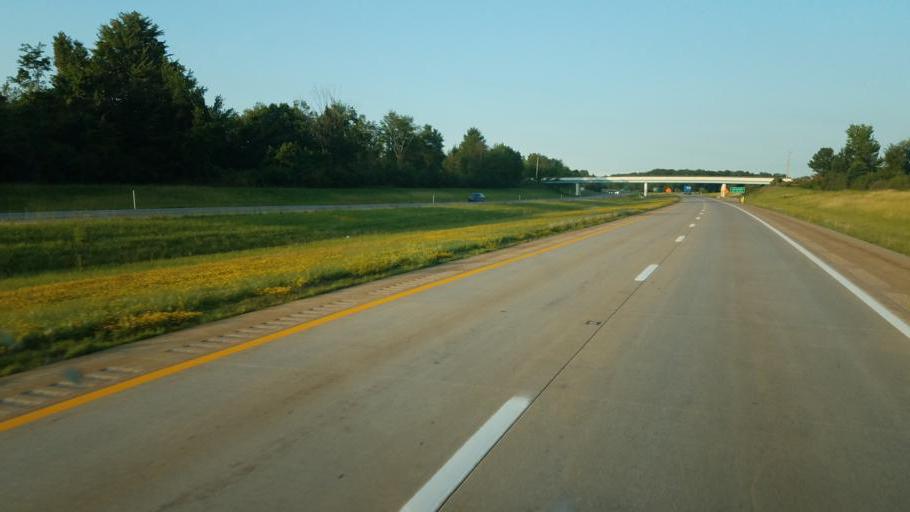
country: US
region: Ohio
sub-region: Ashtabula County
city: Geneva
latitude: 41.7722
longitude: -80.8874
